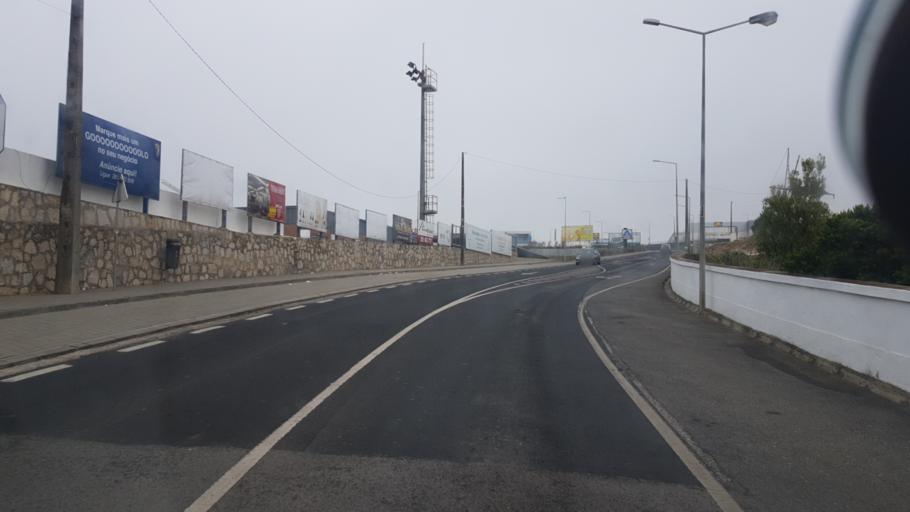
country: PT
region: Lisbon
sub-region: Mafra
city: Ericeira
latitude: 38.9658
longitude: -9.4119
